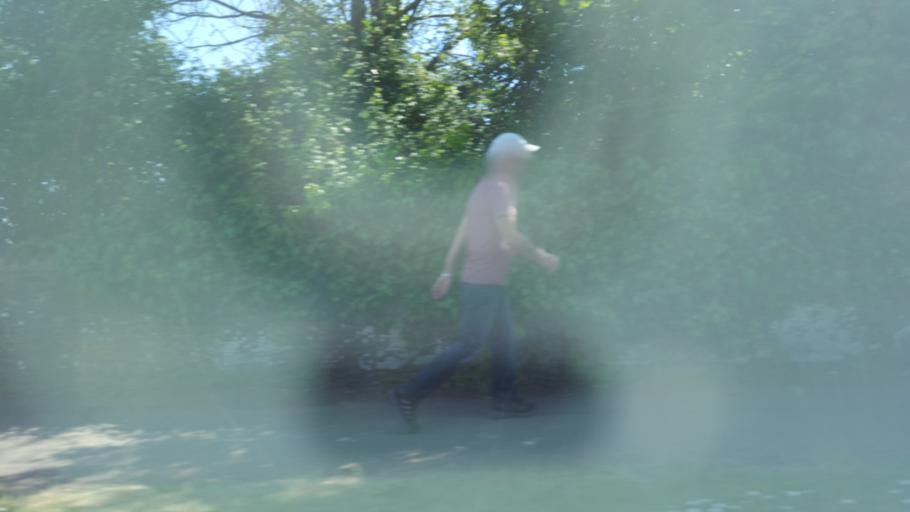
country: GB
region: England
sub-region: South Gloucestershire
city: Winterbourne
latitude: 51.5234
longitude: -2.5133
